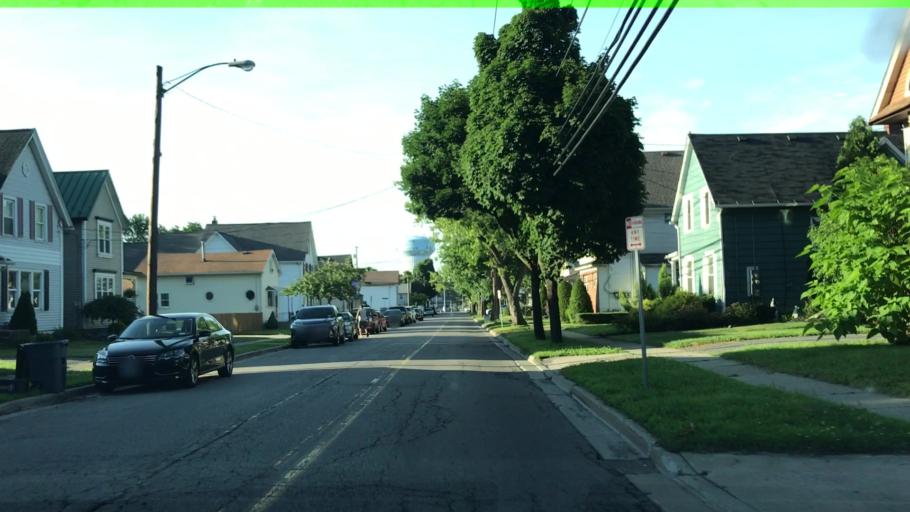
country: US
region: New York
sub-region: Erie County
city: Lancaster
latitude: 42.8971
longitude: -78.6749
